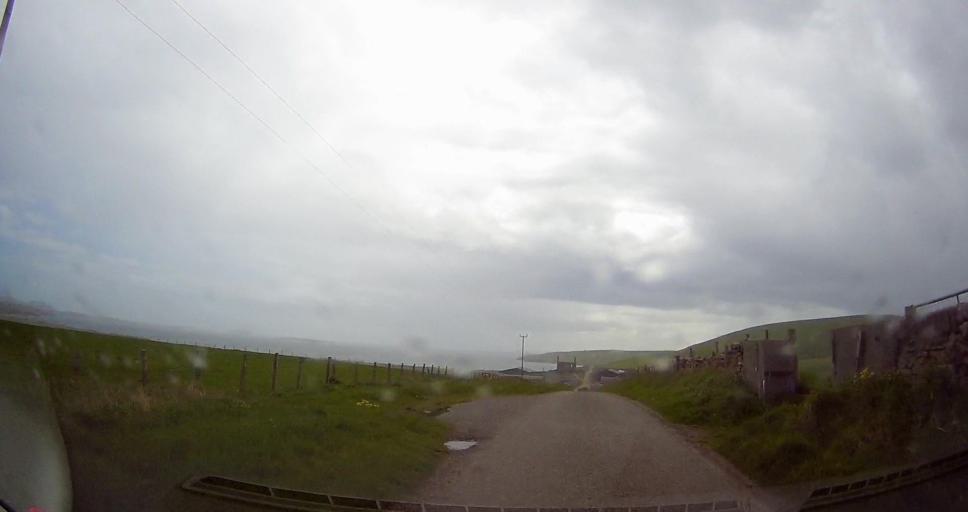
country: GB
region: Scotland
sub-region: Shetland Islands
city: Sandwick
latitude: 59.9057
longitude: -1.3352
